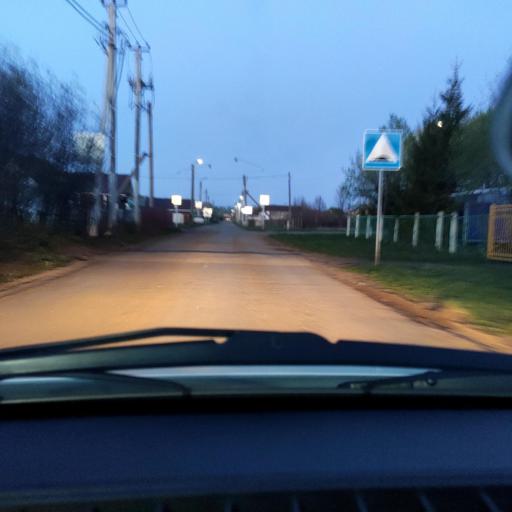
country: RU
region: Bashkortostan
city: Mikhaylovka
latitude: 54.8661
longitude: 55.7374
